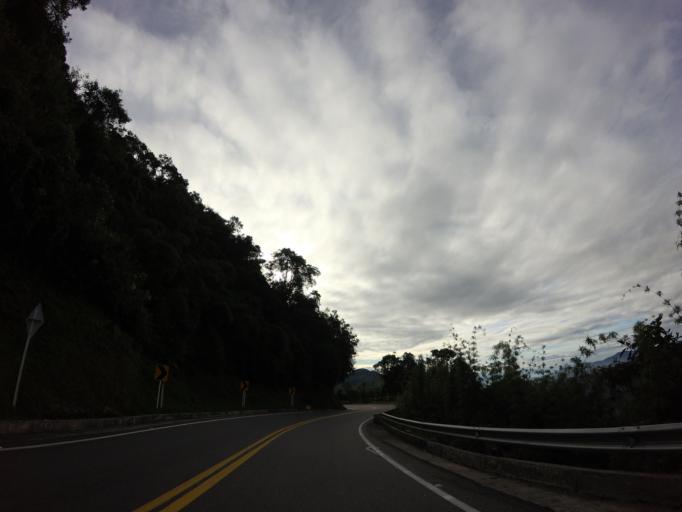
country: CO
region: Tolima
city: Herveo
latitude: 5.1055
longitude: -75.2575
